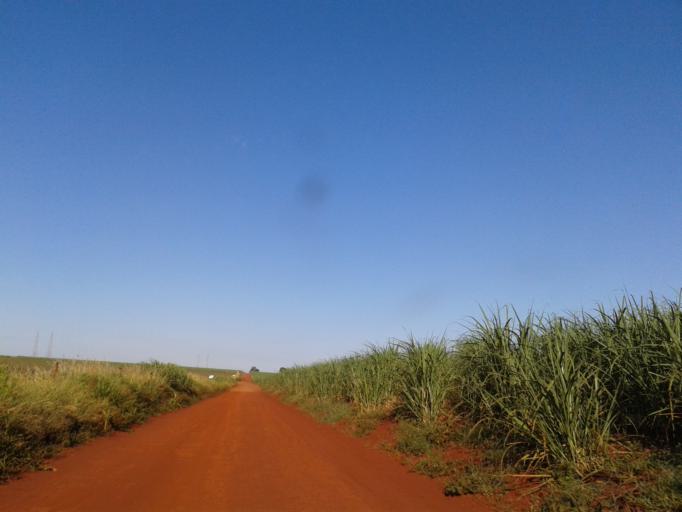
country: BR
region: Minas Gerais
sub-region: Centralina
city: Centralina
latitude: -18.6723
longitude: -49.2733
